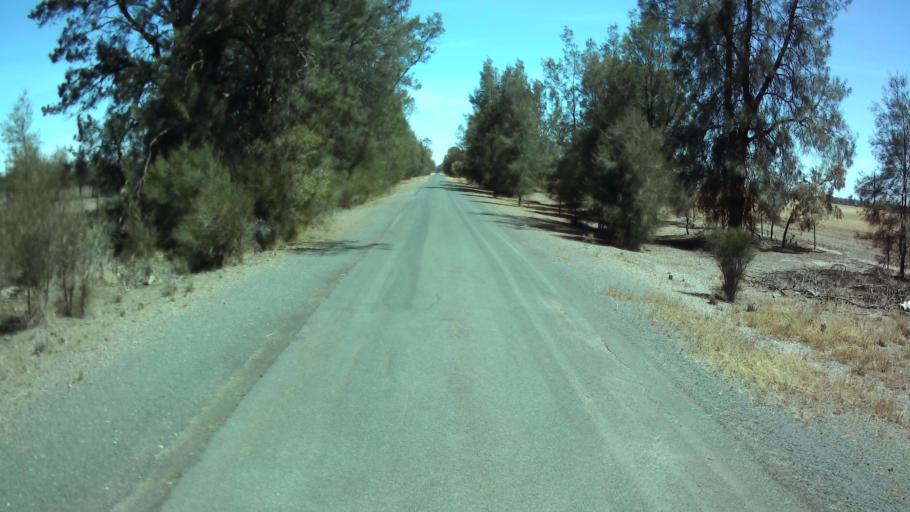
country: AU
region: New South Wales
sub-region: Weddin
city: Grenfell
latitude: -33.8852
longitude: 147.6893
